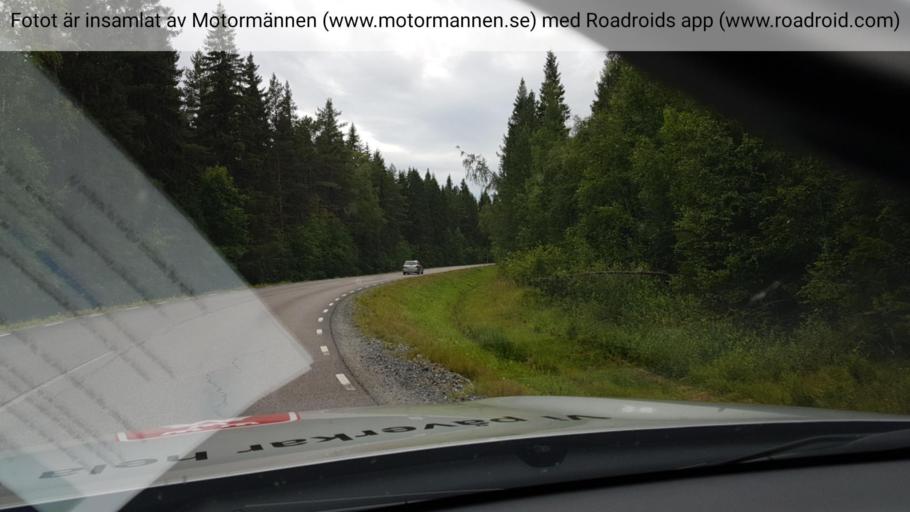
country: SE
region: Norrbotten
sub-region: Lulea Kommun
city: Gammelstad
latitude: 65.6572
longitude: 22.0520
